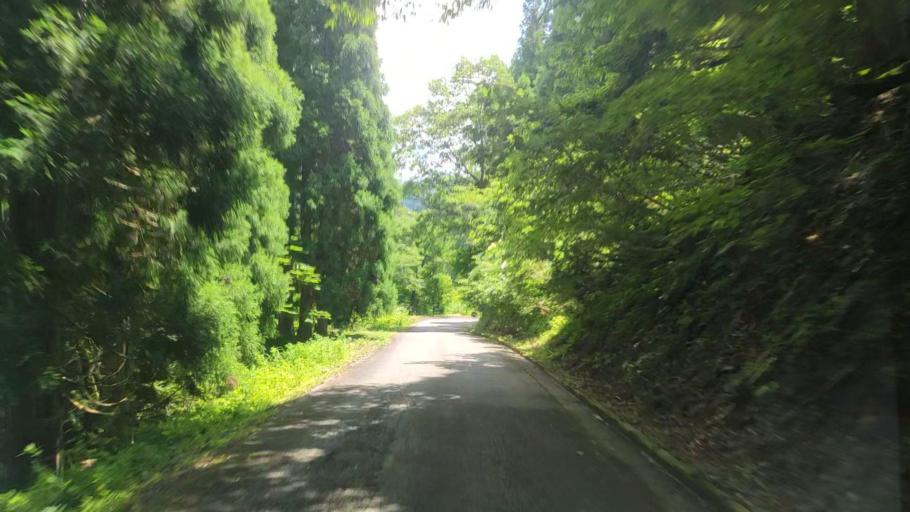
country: JP
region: Fukui
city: Ono
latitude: 35.8176
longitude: 136.4567
